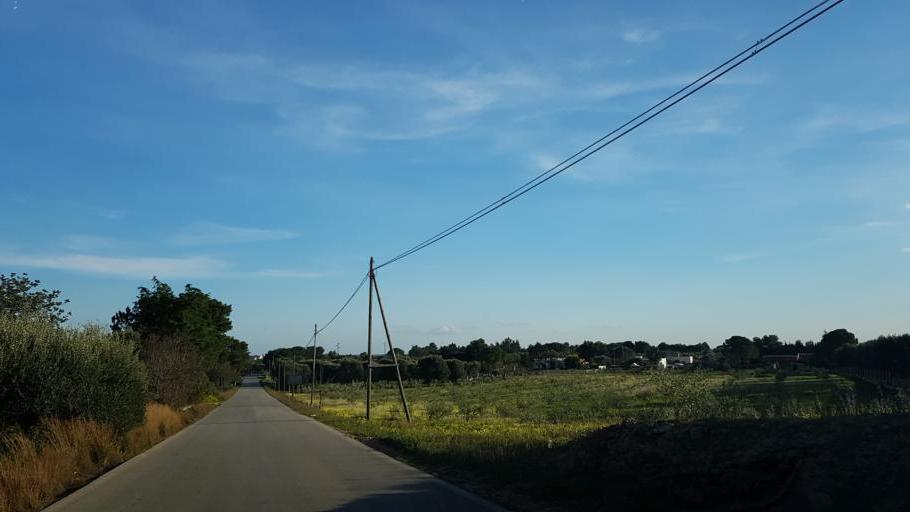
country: IT
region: Apulia
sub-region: Provincia di Brindisi
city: San Vito dei Normanni
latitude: 40.6798
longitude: 17.7726
